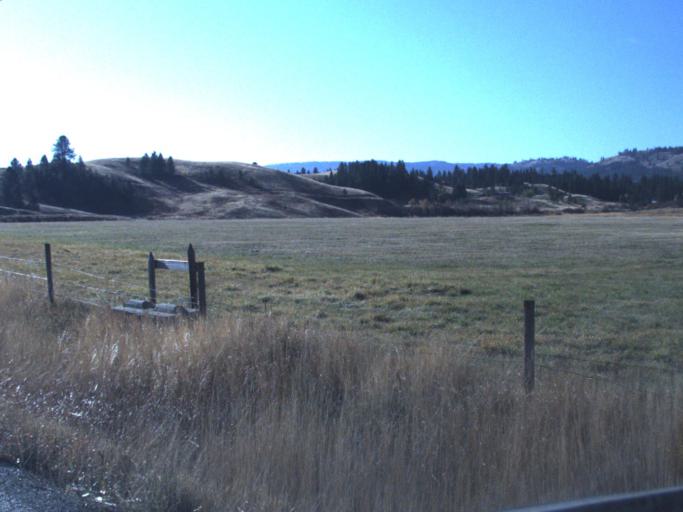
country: US
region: Washington
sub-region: Ferry County
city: Republic
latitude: 48.7717
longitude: -118.6467
